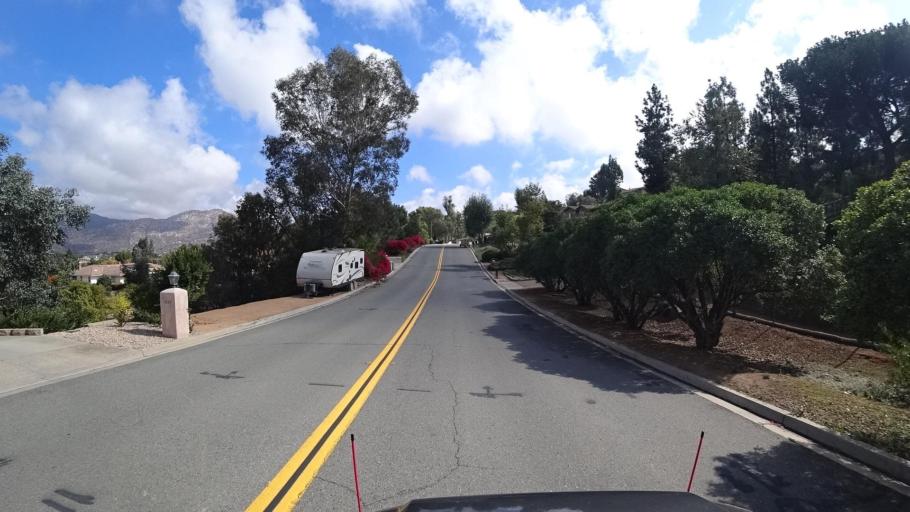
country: US
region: California
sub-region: San Diego County
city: Granite Hills
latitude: 32.7769
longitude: -116.9031
